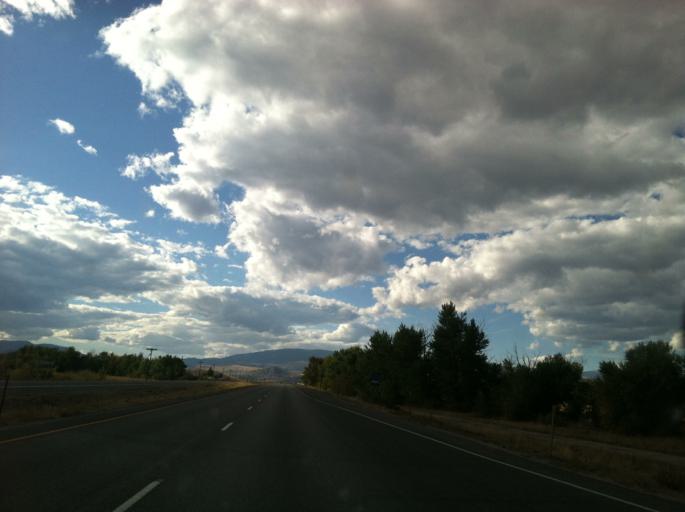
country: US
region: Montana
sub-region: Deer Lodge County
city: Anaconda
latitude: 46.1079
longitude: -112.8504
